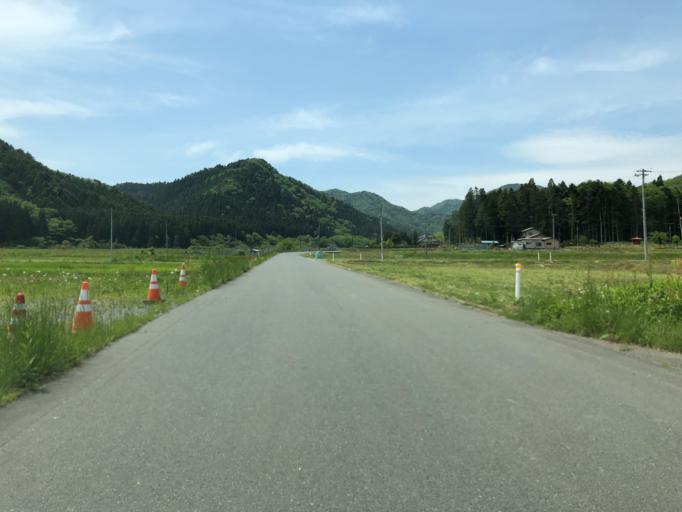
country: JP
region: Fukushima
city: Namie
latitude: 37.6895
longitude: 140.9083
